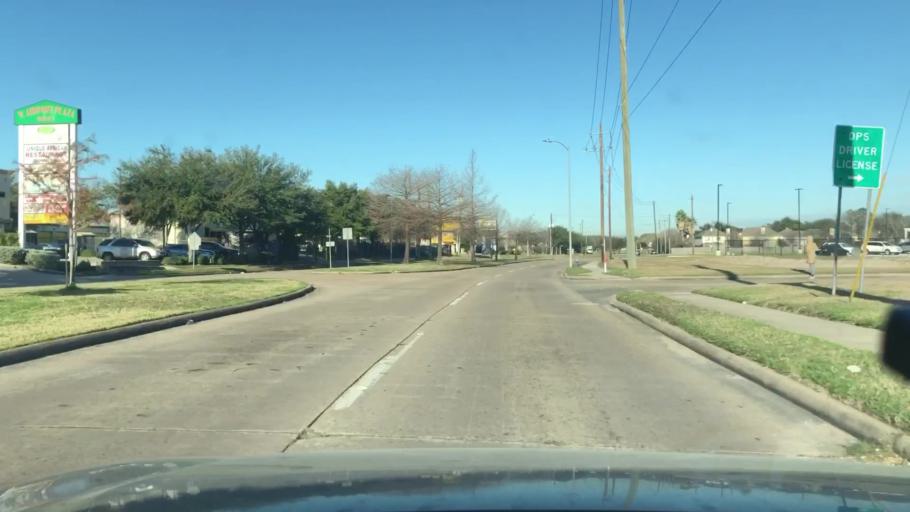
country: US
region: Texas
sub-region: Fort Bend County
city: Missouri City
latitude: 29.6424
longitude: -95.5288
